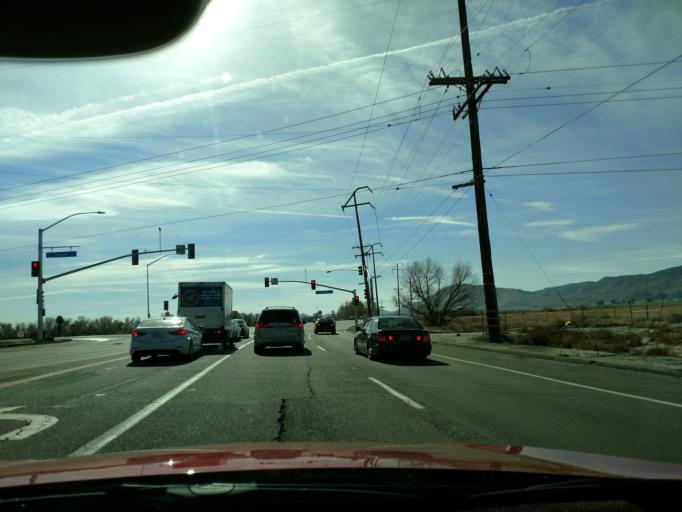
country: US
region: California
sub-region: Riverside County
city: San Jacinto
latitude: 33.8215
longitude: -117.0039
